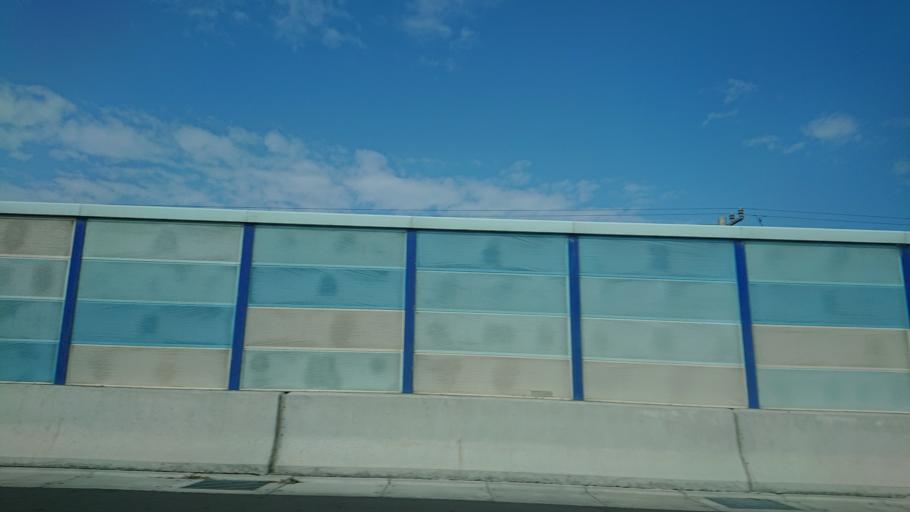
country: TW
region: Taiwan
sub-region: Changhua
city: Chang-hua
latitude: 23.9572
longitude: 120.3333
